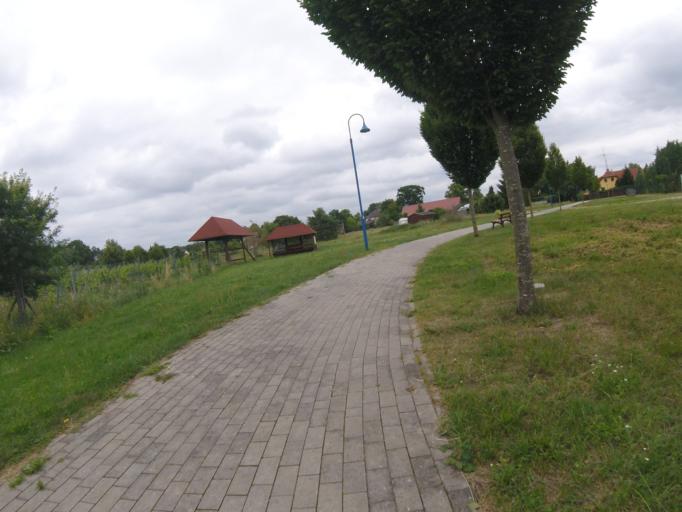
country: DE
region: Brandenburg
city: Bestensee
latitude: 52.2445
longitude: 13.6255
